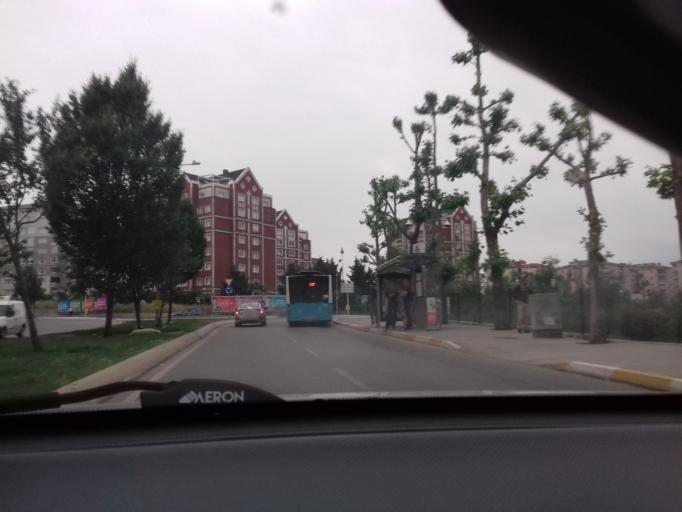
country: TR
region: Istanbul
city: Sultanbeyli
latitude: 40.9285
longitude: 29.2968
